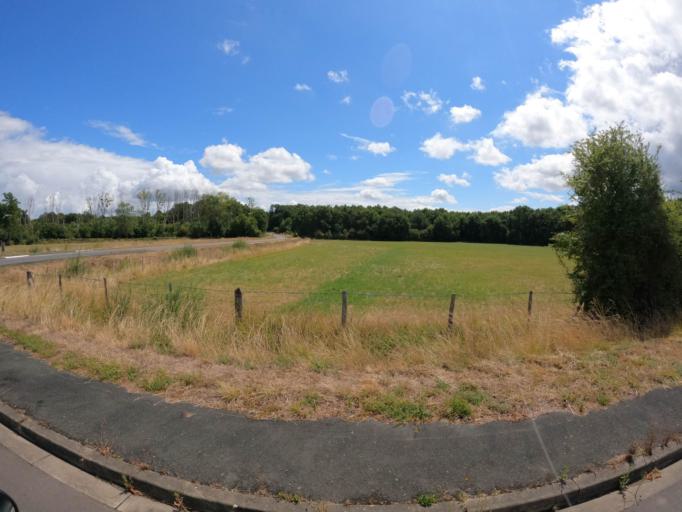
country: FR
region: Pays de la Loire
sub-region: Departement de Maine-et-Loire
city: Feneu
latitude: 47.5650
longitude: -0.5953
